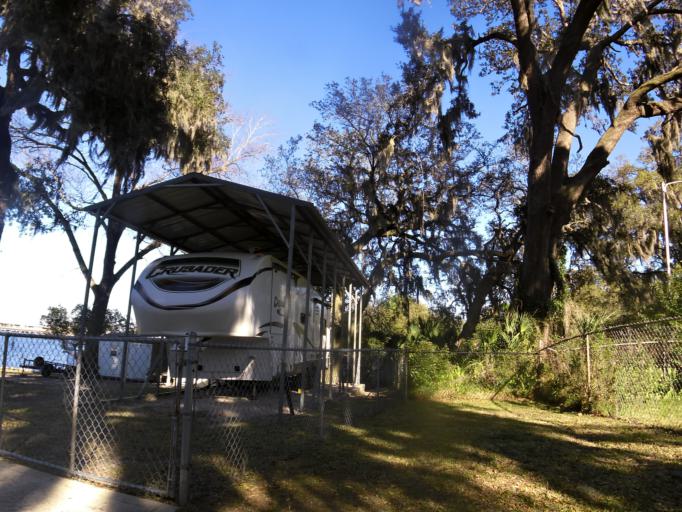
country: US
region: Florida
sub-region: Duval County
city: Jacksonville
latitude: 30.3884
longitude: -81.6537
